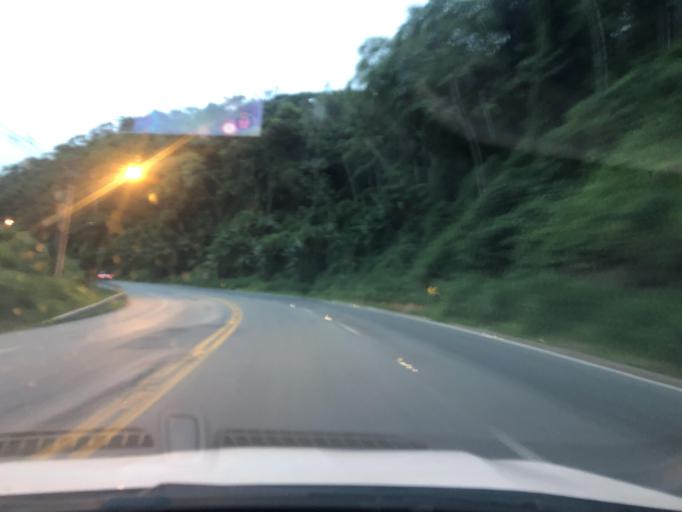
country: BR
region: Santa Catarina
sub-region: Pomerode
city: Pomerode
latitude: -26.7491
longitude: -49.0697
